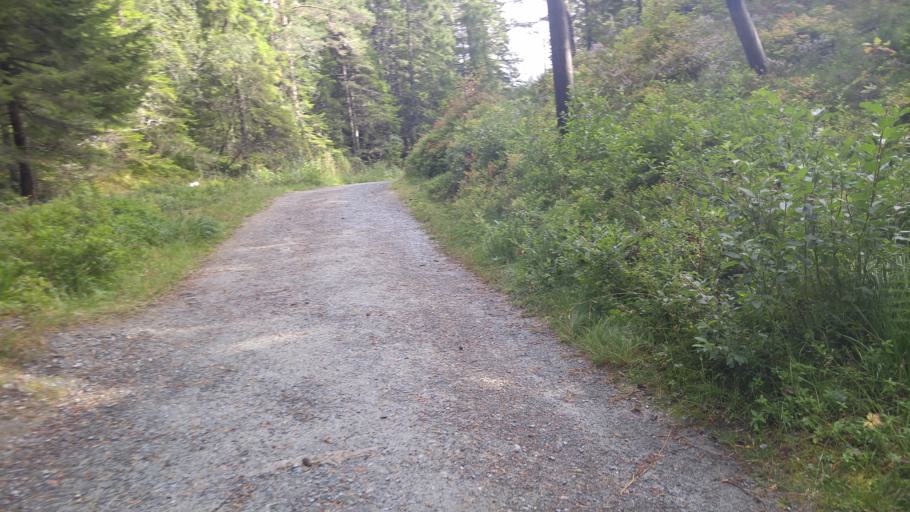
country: NO
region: Sor-Trondelag
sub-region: Trondheim
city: Trondheim
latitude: 63.4131
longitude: 10.3299
